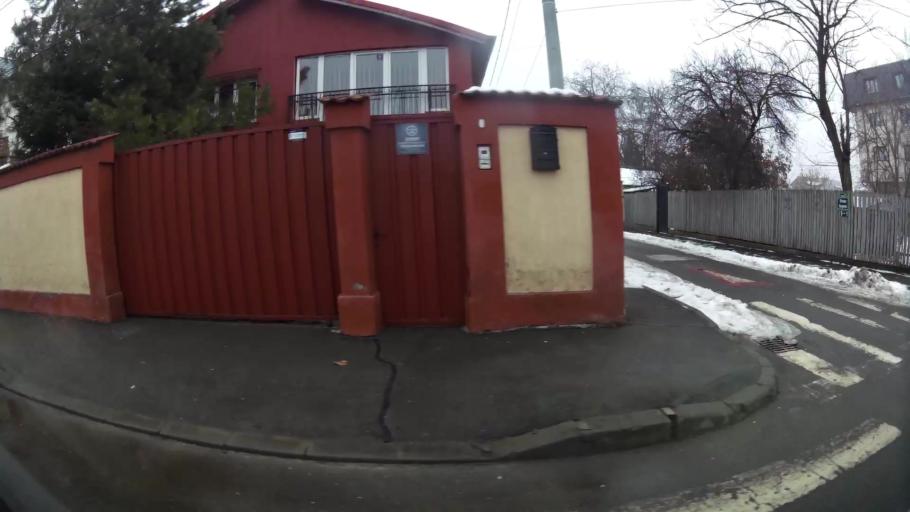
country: RO
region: Ilfov
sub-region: Comuna Chiajna
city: Rosu
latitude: 44.4423
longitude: 26.0108
